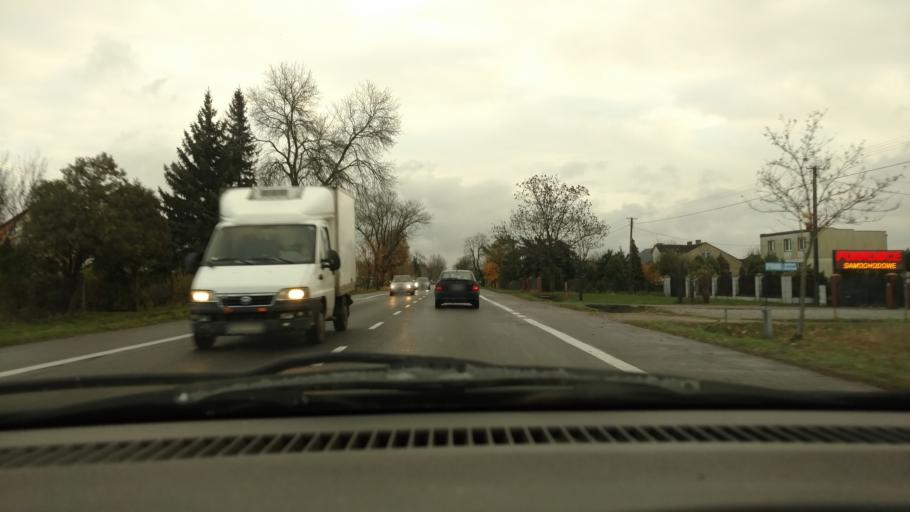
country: PL
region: Lodz Voivodeship
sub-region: Powiat laski
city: Sedziejowice
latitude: 51.5914
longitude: 19.0295
